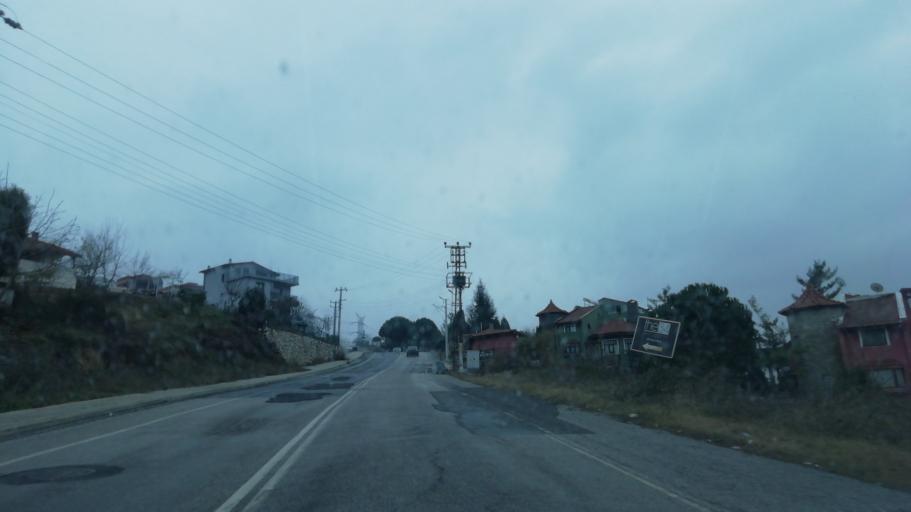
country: TR
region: Sakarya
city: Kazimpasa
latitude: 40.7429
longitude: 30.3111
